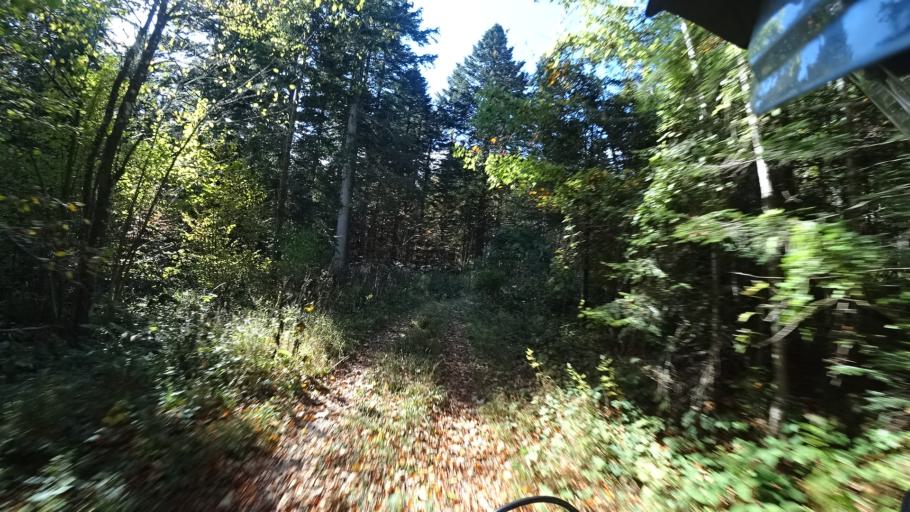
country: HR
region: Karlovacka
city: Plaski
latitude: 45.0656
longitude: 15.3163
